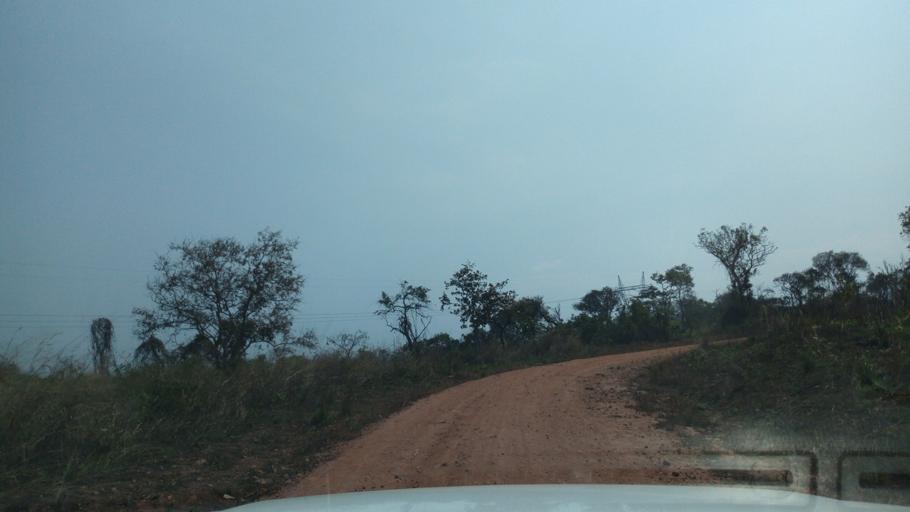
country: CD
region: Katanga
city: Kalemie
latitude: -5.6160
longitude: 29.0511
